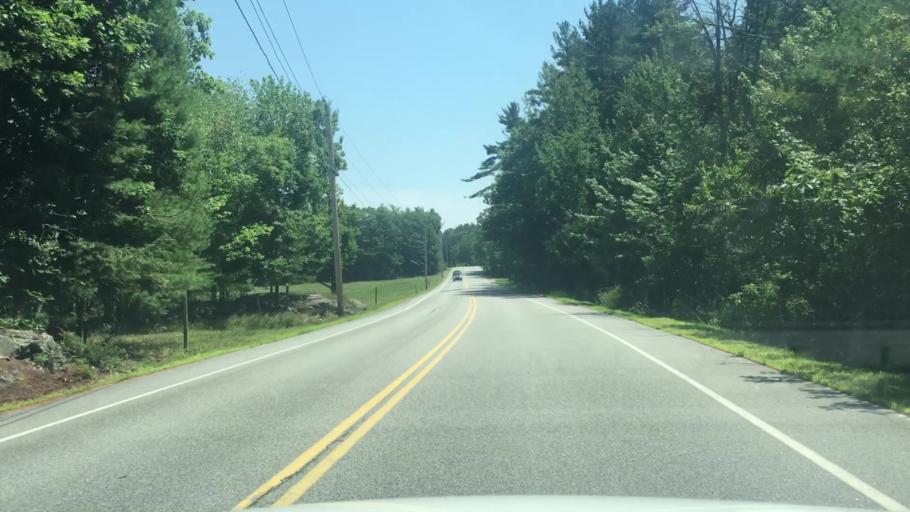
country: US
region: Maine
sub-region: Cumberland County
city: Falmouth
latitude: 43.7448
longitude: -70.2571
